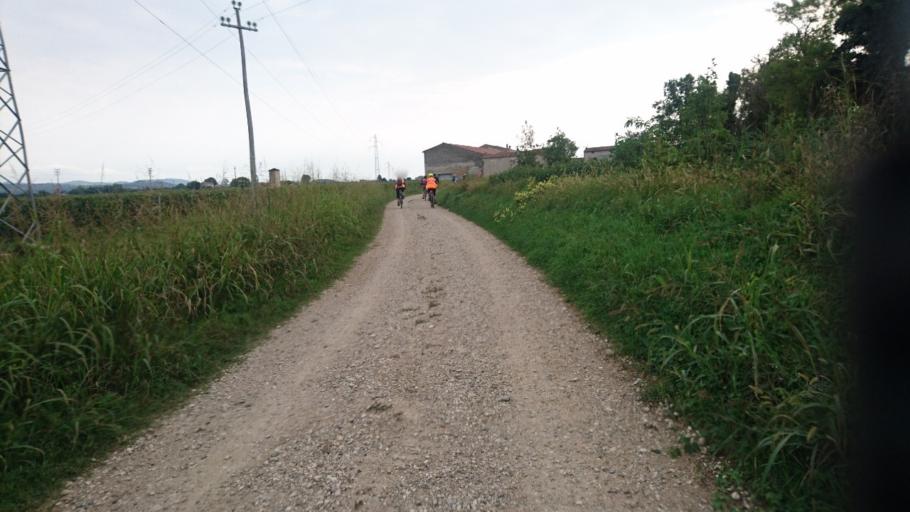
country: IT
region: Veneto
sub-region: Provincia di Verona
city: Monticelli-Fontana
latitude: 45.4019
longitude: 11.1316
